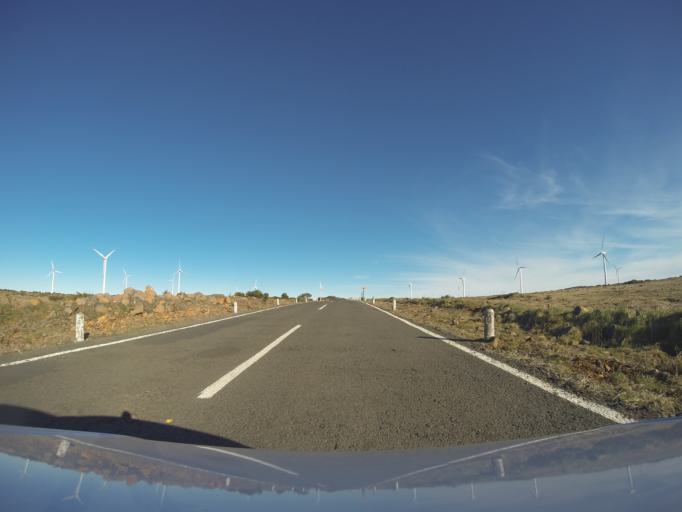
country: PT
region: Madeira
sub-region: Sao Vicente
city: Sao Vicente
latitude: 32.7619
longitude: -17.0678
